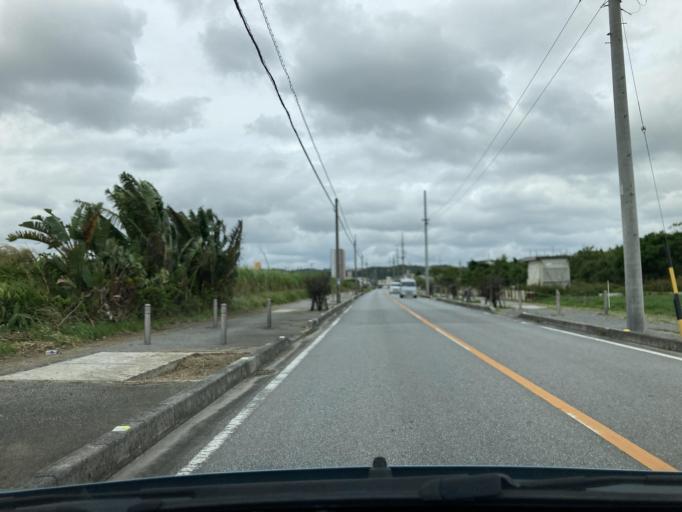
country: JP
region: Okinawa
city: Ginowan
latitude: 26.2223
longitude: 127.7721
